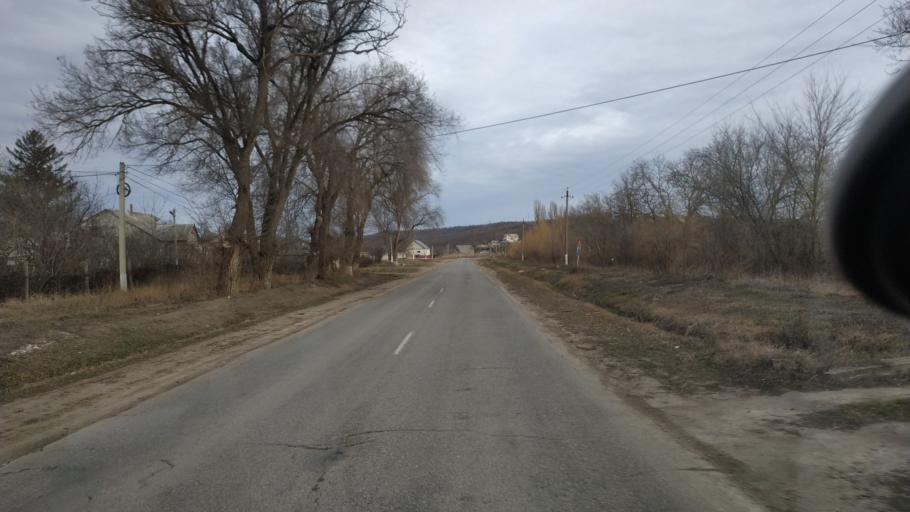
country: MD
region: Chisinau
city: Vadul lui Voda
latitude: 47.1357
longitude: 29.0613
